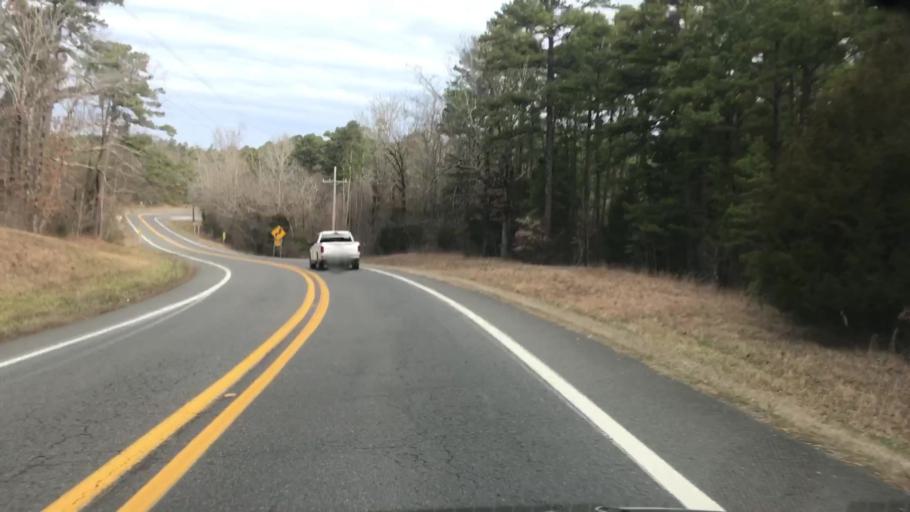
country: US
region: Arkansas
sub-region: Montgomery County
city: Mount Ida
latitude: 34.5907
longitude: -93.6645
